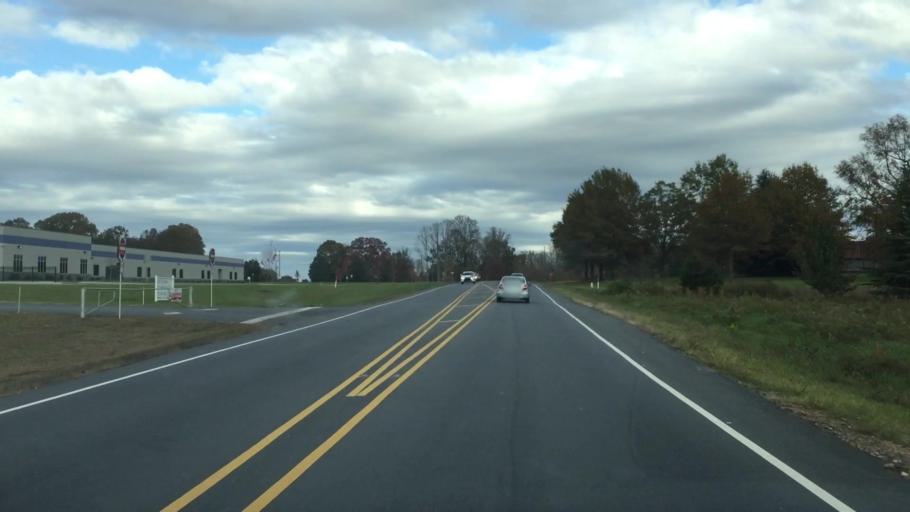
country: US
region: North Carolina
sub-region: Guilford County
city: Summerfield
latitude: 36.2607
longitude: -79.8693
